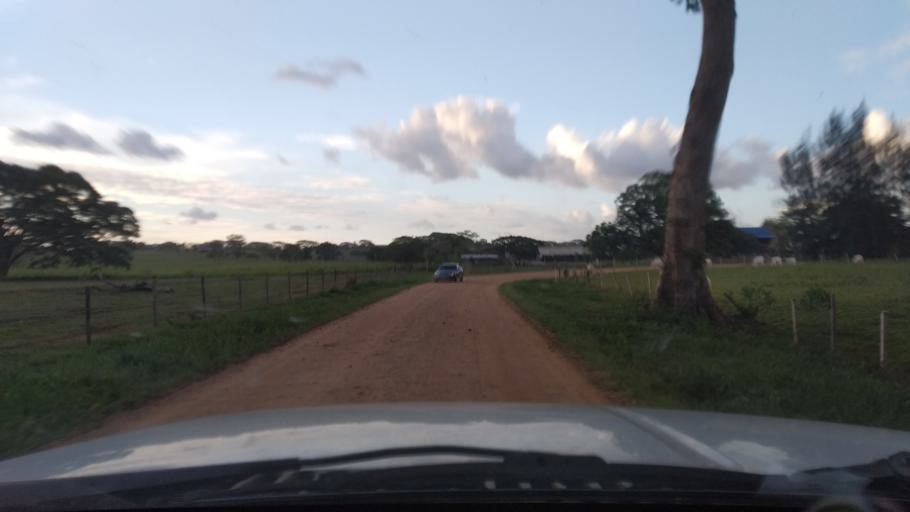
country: BZ
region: Cayo
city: San Ignacio
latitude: 17.2231
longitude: -88.9983
